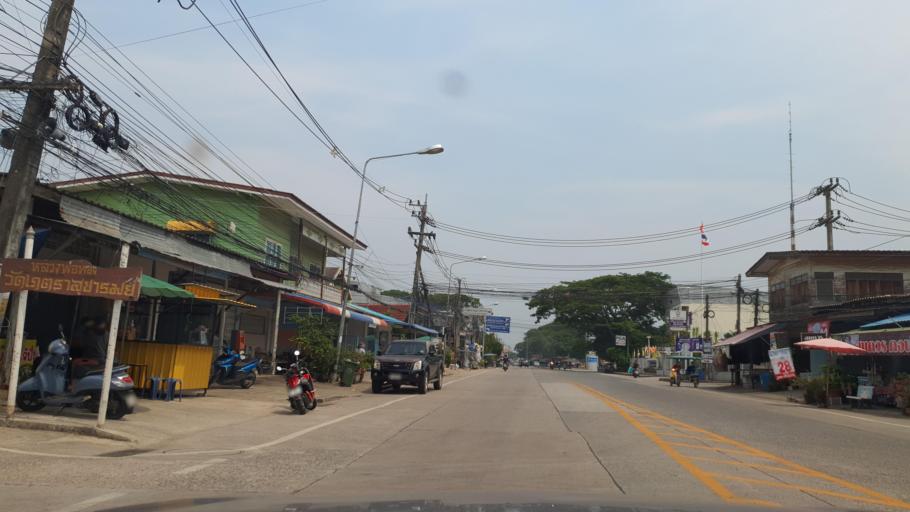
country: TH
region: Rayong
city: Rayong
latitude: 12.6239
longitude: 101.4256
